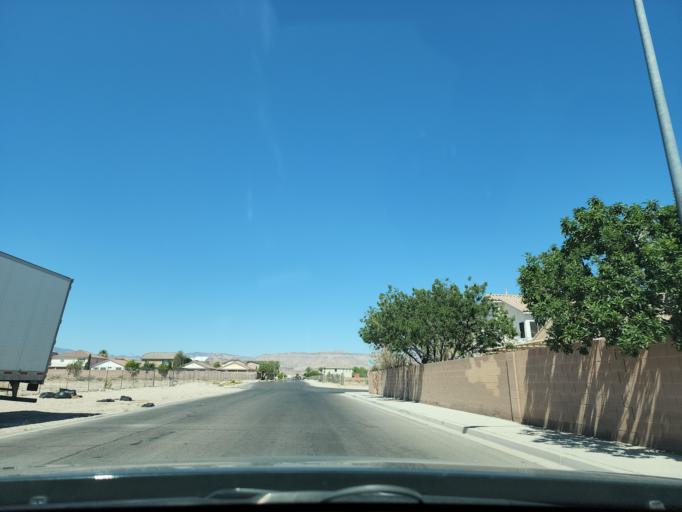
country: US
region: Nevada
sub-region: Clark County
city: Spring Valley
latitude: 36.0814
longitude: -115.2556
